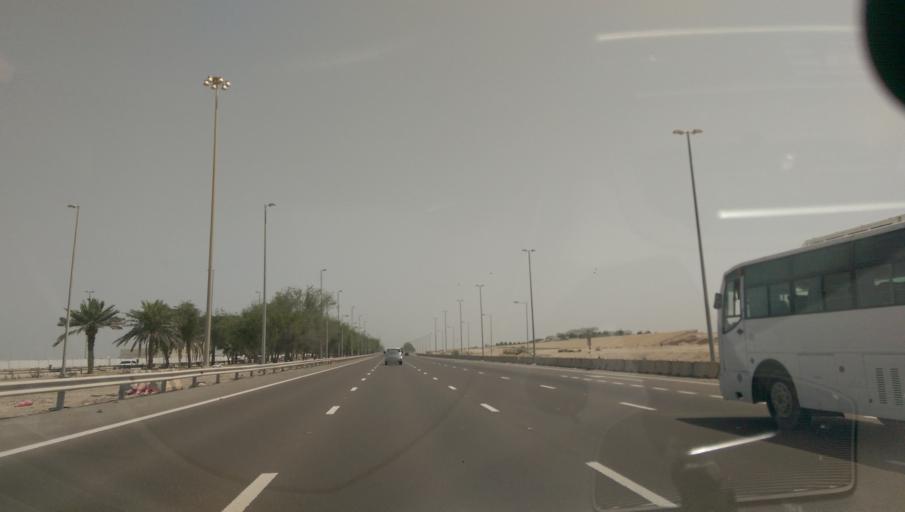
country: AE
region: Abu Dhabi
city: Abu Dhabi
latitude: 24.4314
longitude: 54.6780
